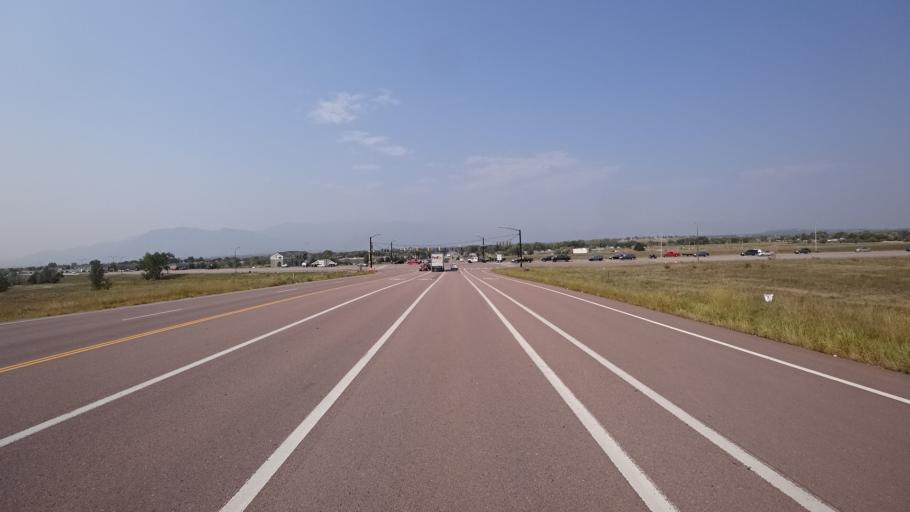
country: US
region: Colorado
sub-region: El Paso County
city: Cimarron Hills
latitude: 38.8247
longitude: -104.7235
